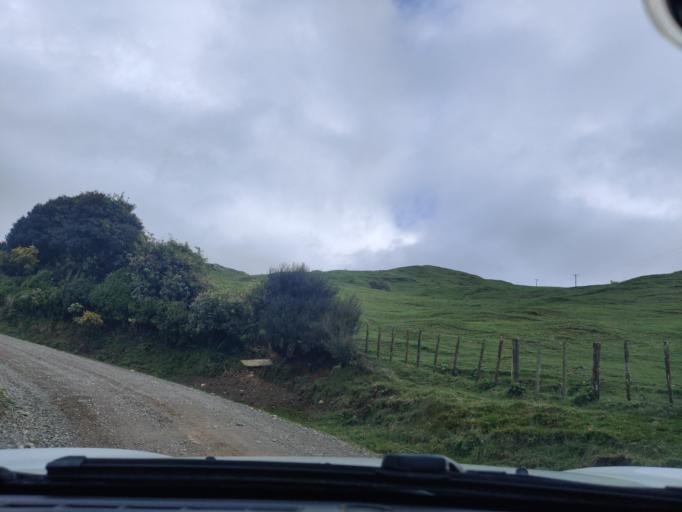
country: NZ
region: Manawatu-Wanganui
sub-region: Palmerston North City
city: Palmerston North
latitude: -40.2784
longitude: 175.8570
